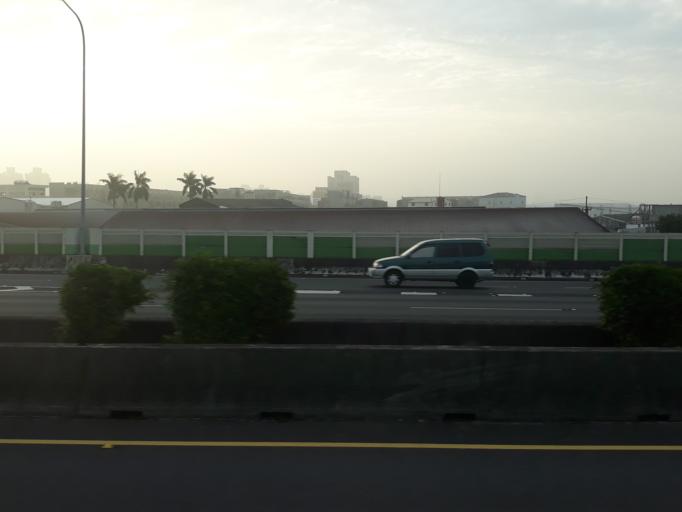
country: TW
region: Taiwan
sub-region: Taichung City
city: Taichung
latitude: 24.2033
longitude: 120.6519
